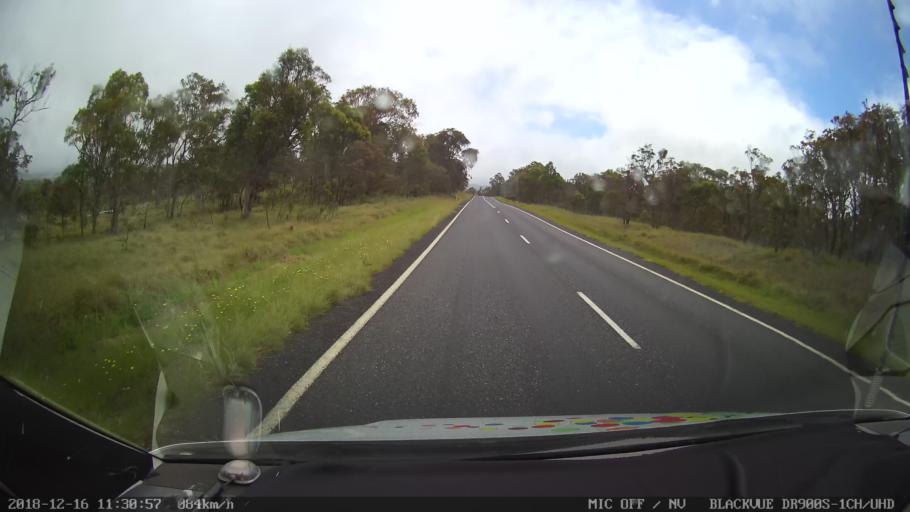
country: AU
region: New South Wales
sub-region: Tenterfield Municipality
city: Carrolls Creek
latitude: -29.0263
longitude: 152.1232
